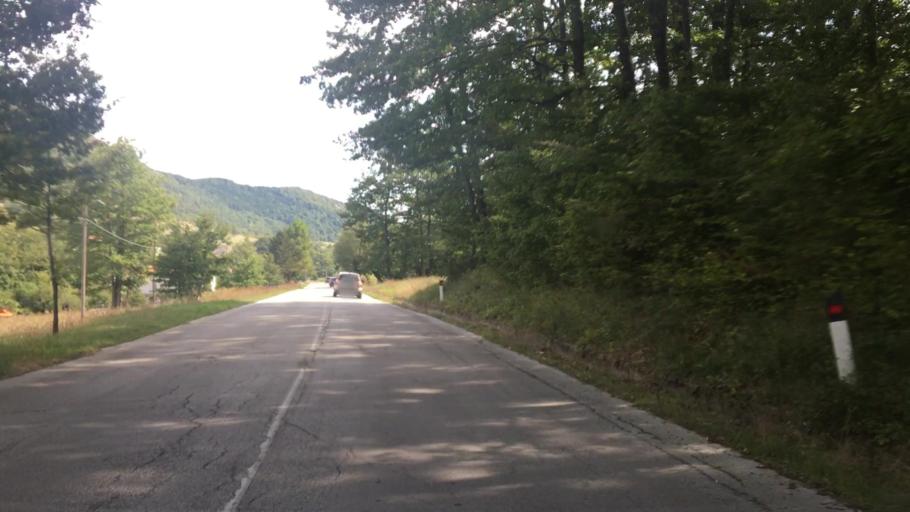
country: IT
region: Molise
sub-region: Provincia di Isernia
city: Carovilli
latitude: 41.7298
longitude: 14.2702
